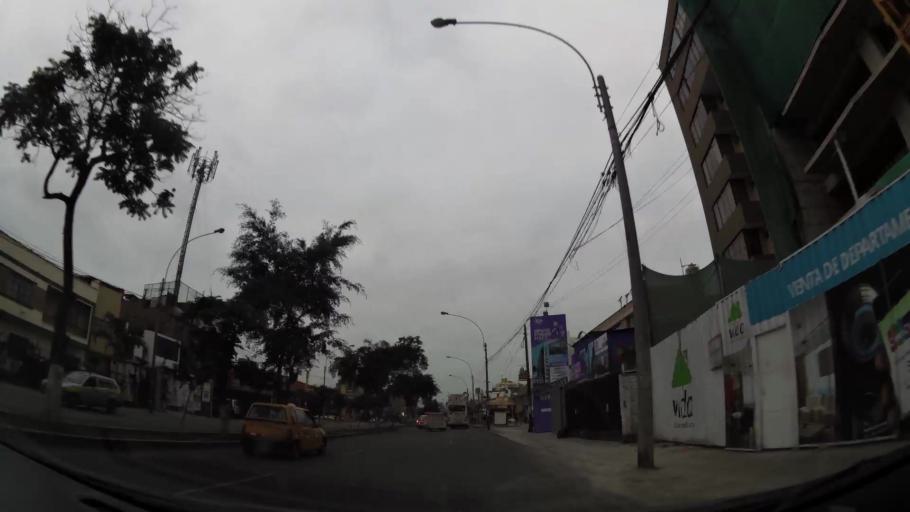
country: PE
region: Lima
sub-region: Lima
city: San Isidro
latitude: -12.0723
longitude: -77.0651
